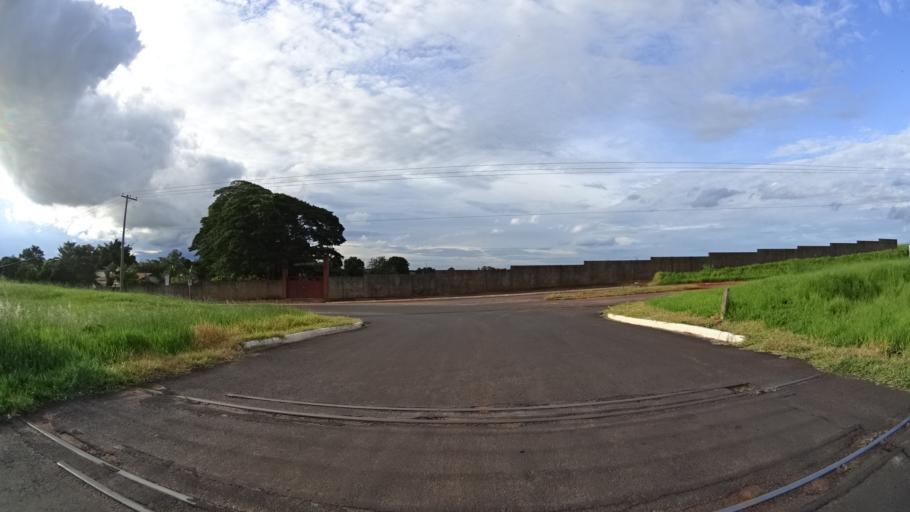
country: BR
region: Sao Paulo
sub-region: Marilia
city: Marilia
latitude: -22.2230
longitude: -49.8936
